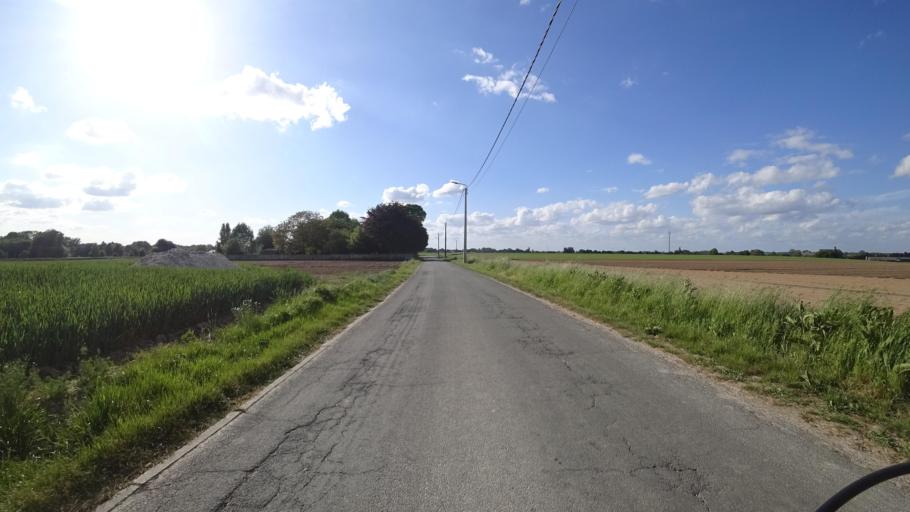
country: BE
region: Wallonia
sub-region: Province de Namur
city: Gembloux
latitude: 50.5435
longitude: 4.7386
